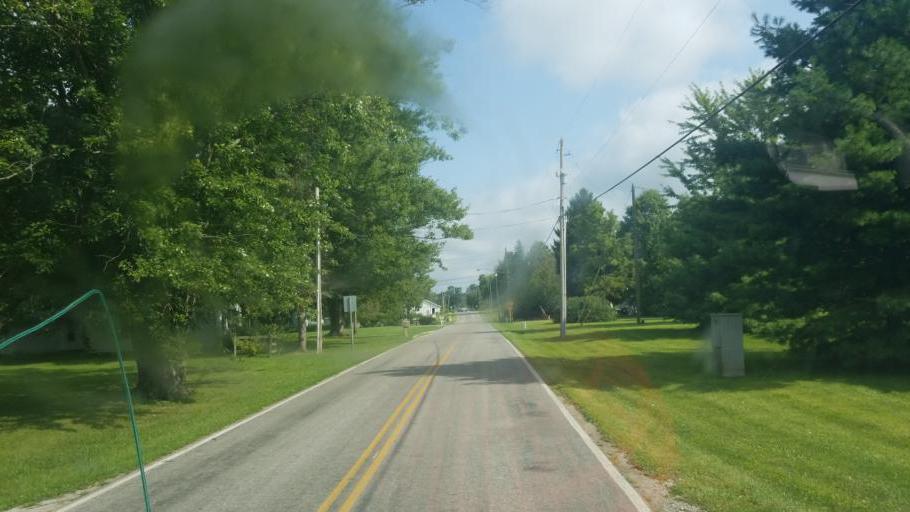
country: US
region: Ohio
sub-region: Morrow County
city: Cardington
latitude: 40.5810
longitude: -82.9967
